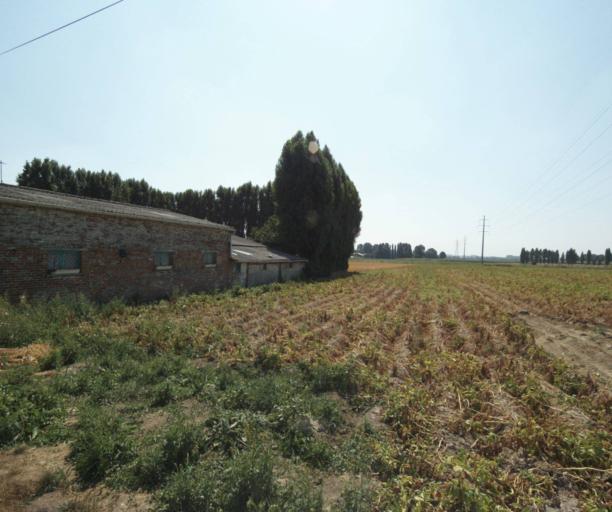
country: FR
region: Nord-Pas-de-Calais
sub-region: Departement du Nord
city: Wervicq-Sud
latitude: 50.7590
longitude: 3.0595
